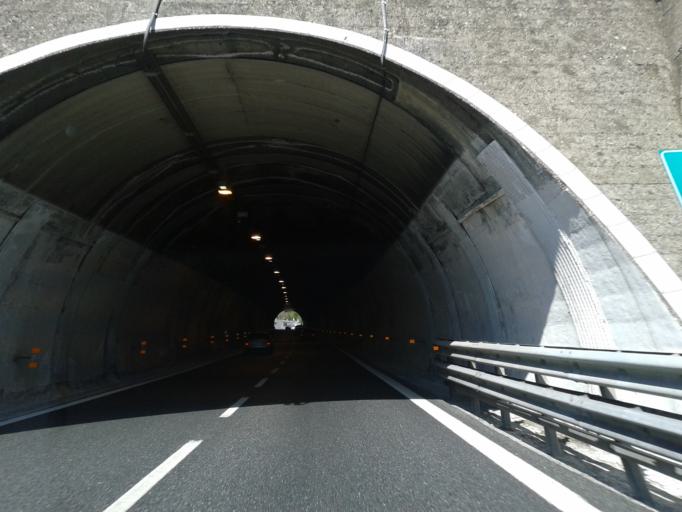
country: IT
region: Liguria
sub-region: Provincia di Genova
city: Chiavari
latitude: 44.3286
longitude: 9.3177
